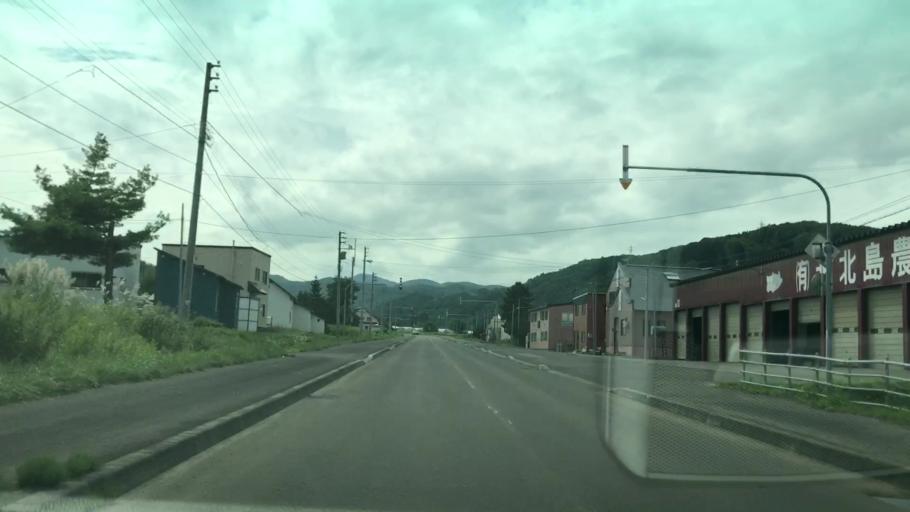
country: JP
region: Hokkaido
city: Yoichi
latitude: 43.1804
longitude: 140.8452
